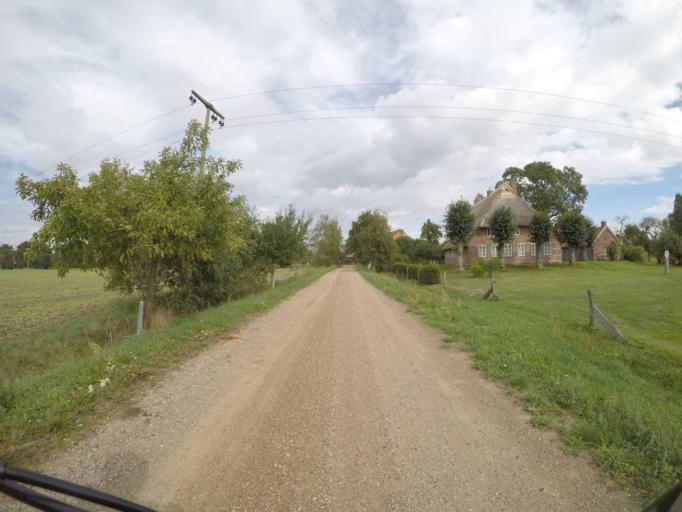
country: DE
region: Lower Saxony
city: Neu Darchau
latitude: 53.2576
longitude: 10.8588
